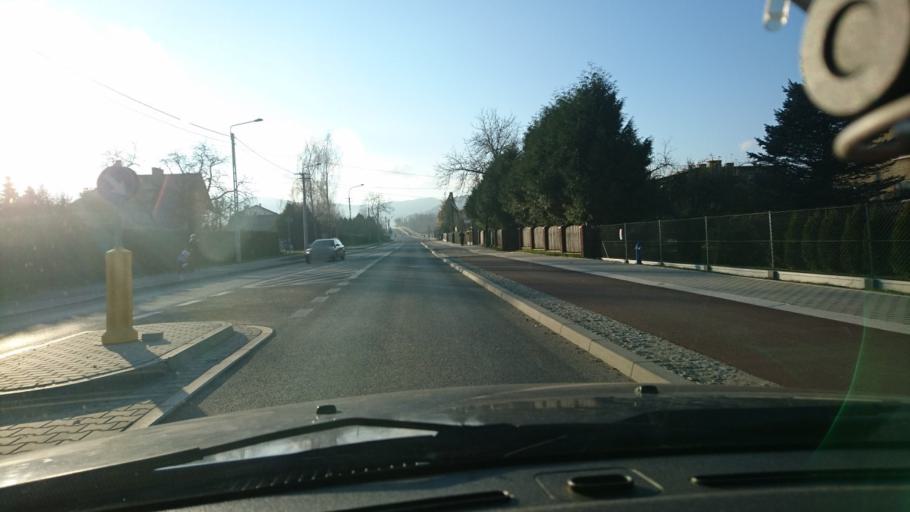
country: PL
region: Silesian Voivodeship
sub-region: Powiat bielski
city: Jaworze
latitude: 49.8154
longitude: 18.9752
